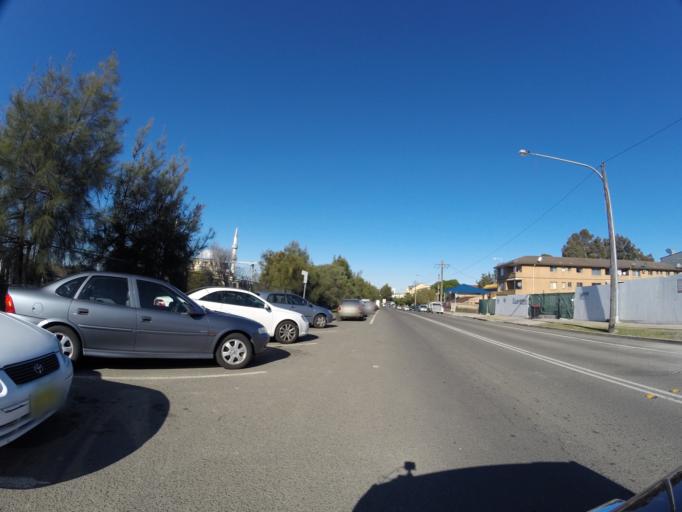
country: AU
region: New South Wales
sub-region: Auburn
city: Auburn
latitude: -33.8516
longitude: 151.0344
